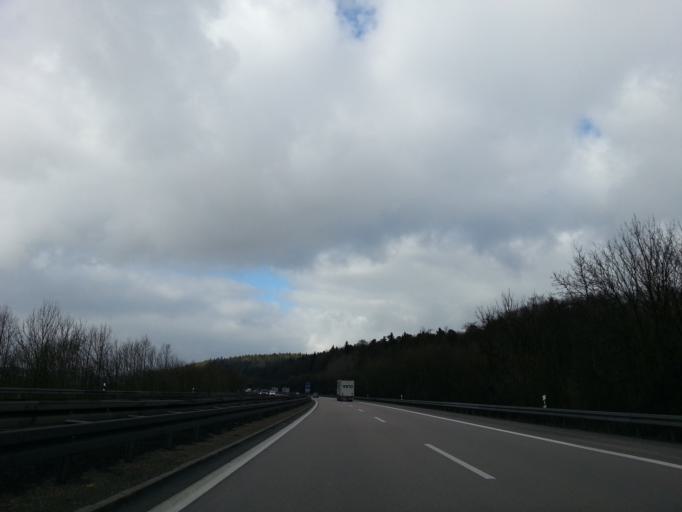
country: DE
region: Bavaria
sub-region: Upper Palatinate
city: Velburg
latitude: 49.2173
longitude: 11.6489
